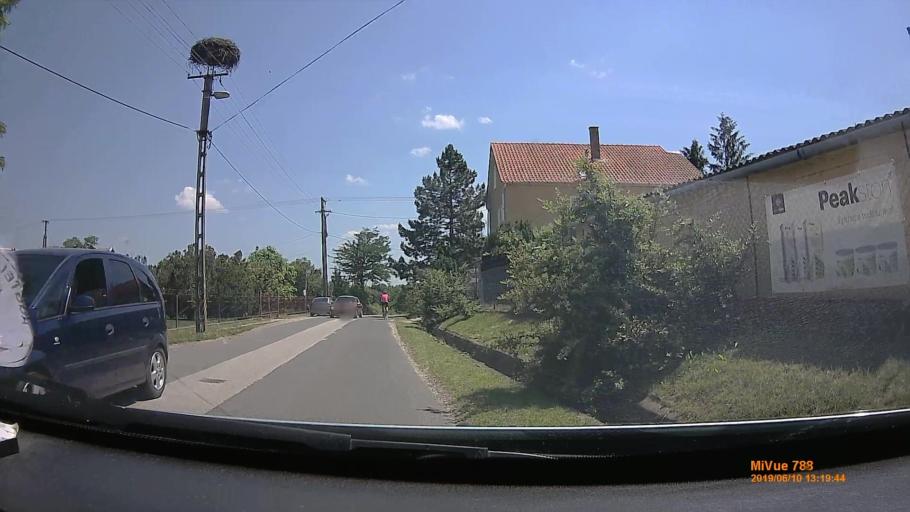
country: HU
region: Borsod-Abauj-Zemplen
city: Tiszaluc
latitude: 48.0403
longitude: 21.0766
